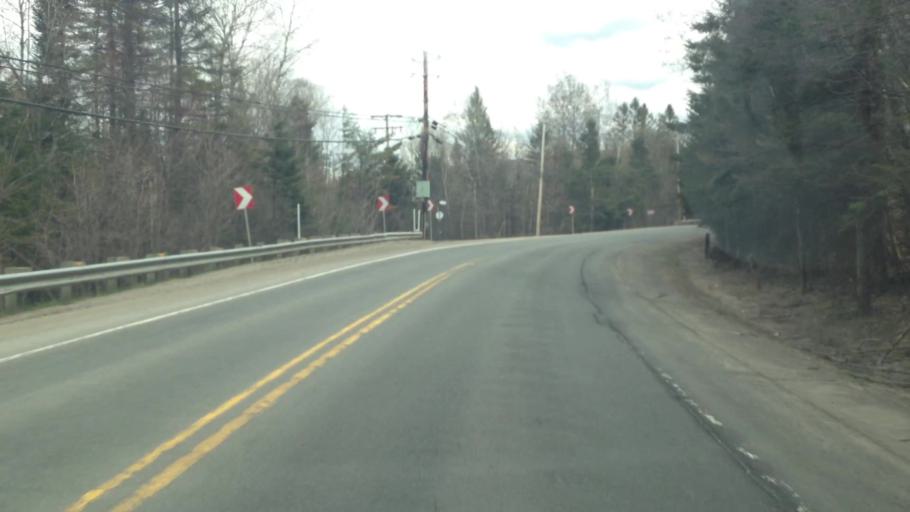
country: CA
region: Quebec
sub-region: Laurentides
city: Sainte-Adele
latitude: 45.9734
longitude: -74.1158
